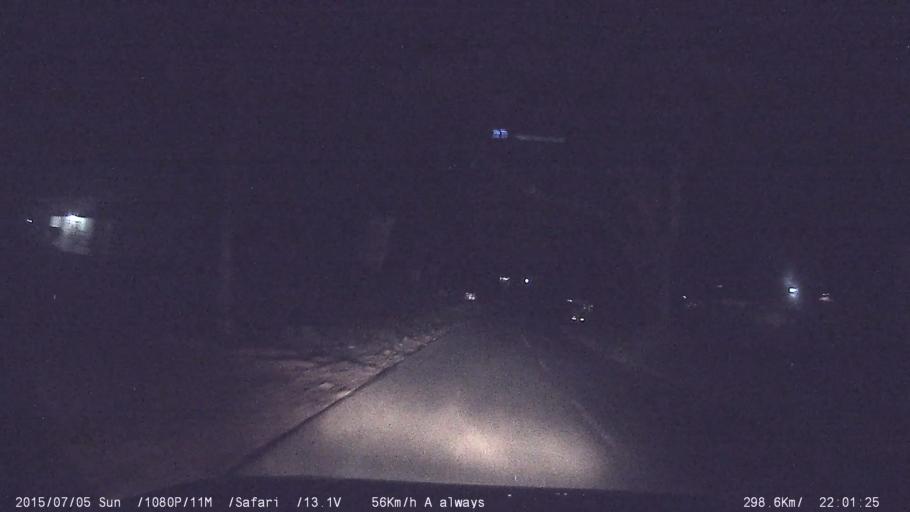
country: IN
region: Kerala
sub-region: Palakkad district
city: Mannarakkat
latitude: 10.9464
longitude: 76.5233
